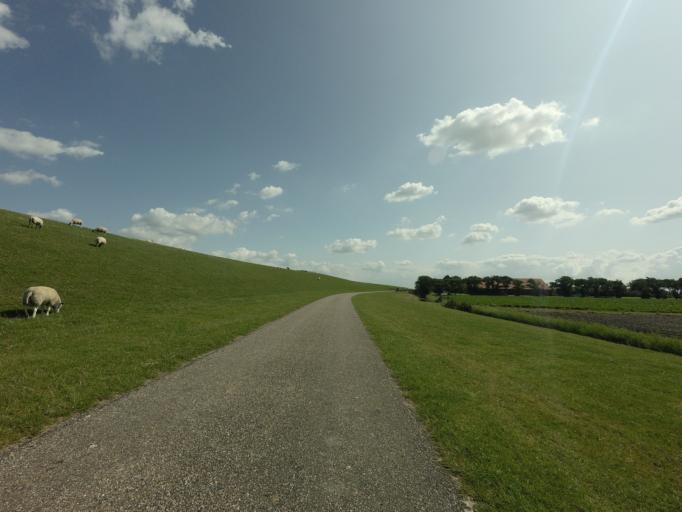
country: NL
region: Friesland
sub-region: Gemeente Ferwerderadiel
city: Hallum
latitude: 53.3236
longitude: 5.7376
